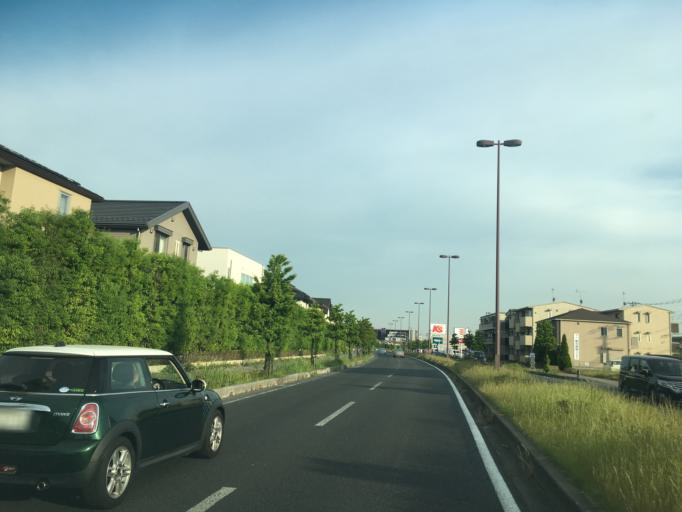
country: JP
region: Saitama
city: Yoshikawa
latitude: 35.8811
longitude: 139.8159
